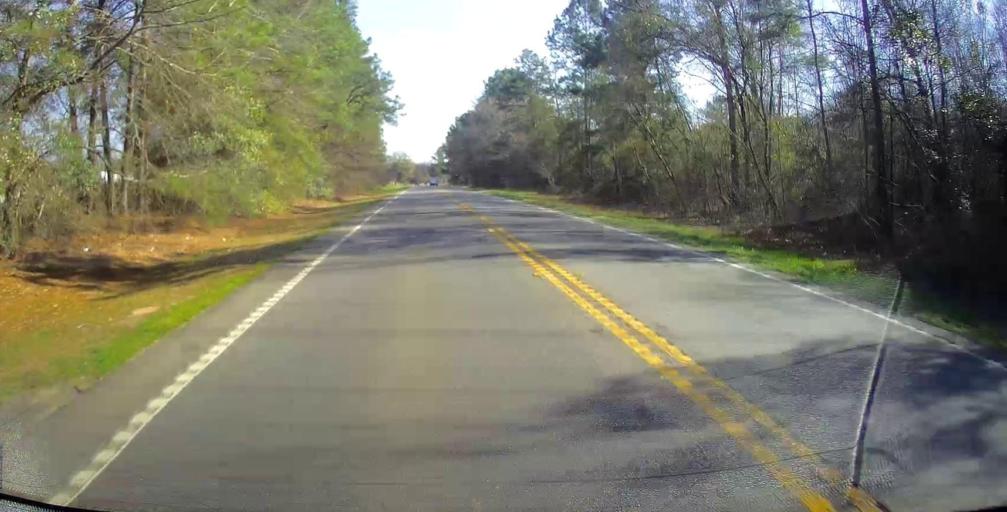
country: US
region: Georgia
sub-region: Macon County
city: Oglethorpe
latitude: 32.3192
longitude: -84.0671
